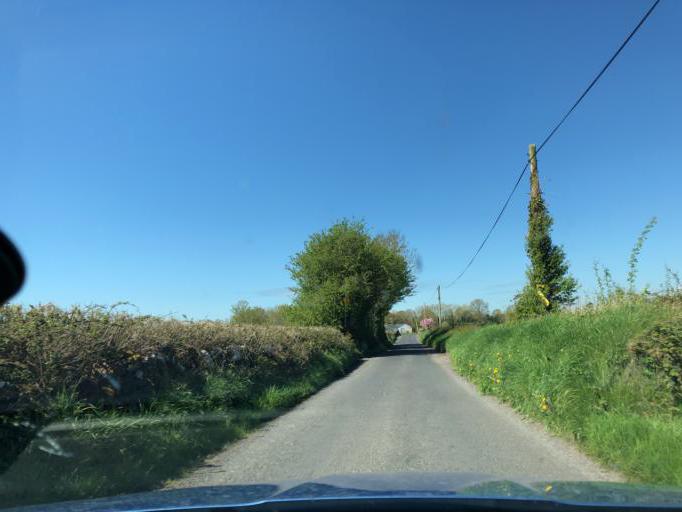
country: IE
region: Connaught
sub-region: County Galway
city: Portumna
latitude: 53.1582
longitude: -8.3022
